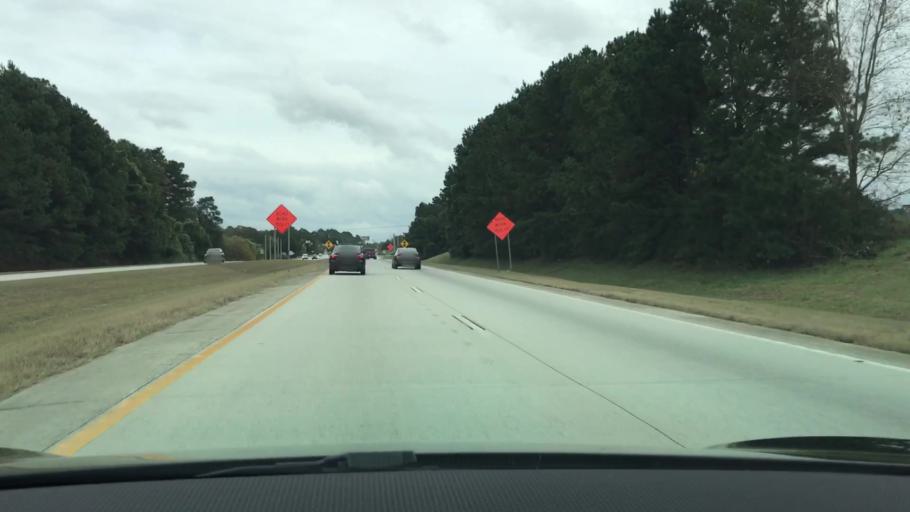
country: US
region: Georgia
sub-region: Barrow County
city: Winder
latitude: 33.9543
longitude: -83.7724
